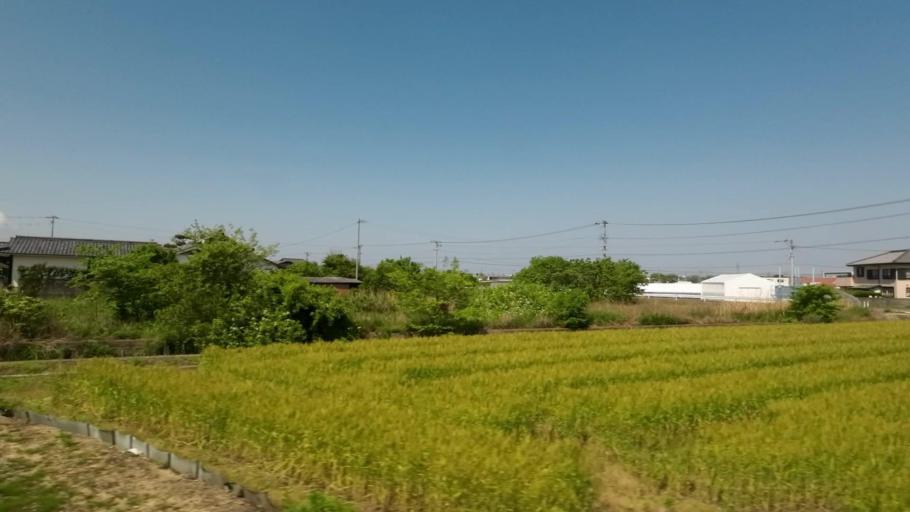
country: JP
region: Kagawa
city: Kan'onjicho
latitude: 34.1105
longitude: 133.6493
